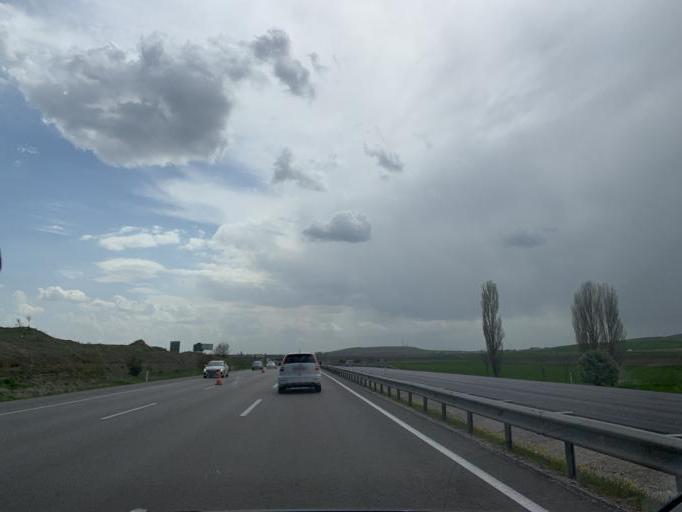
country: TR
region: Ankara
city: Polatli
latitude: 39.6345
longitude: 32.1999
